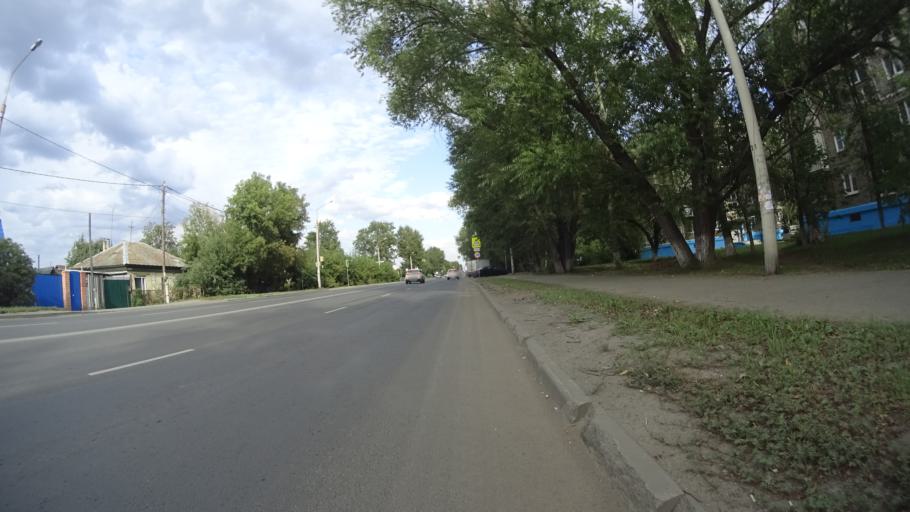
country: RU
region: Chelyabinsk
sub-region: Gorod Chelyabinsk
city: Chelyabinsk
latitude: 55.1985
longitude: 61.3443
